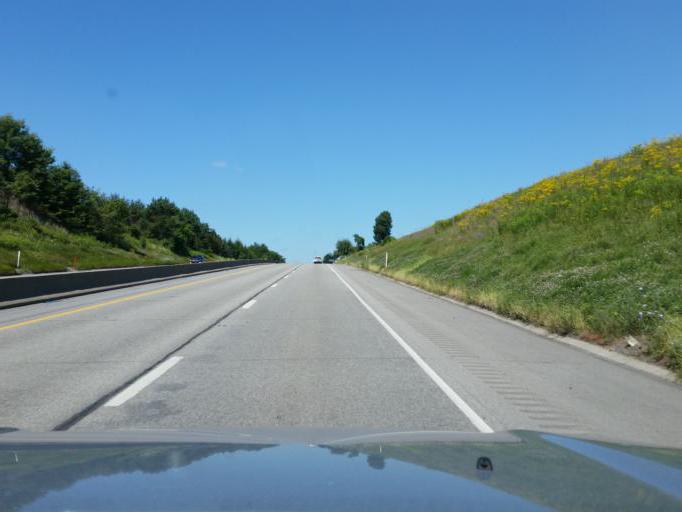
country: US
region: Pennsylvania
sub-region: Cambria County
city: Mundys Corner
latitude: 40.4480
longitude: -78.8176
